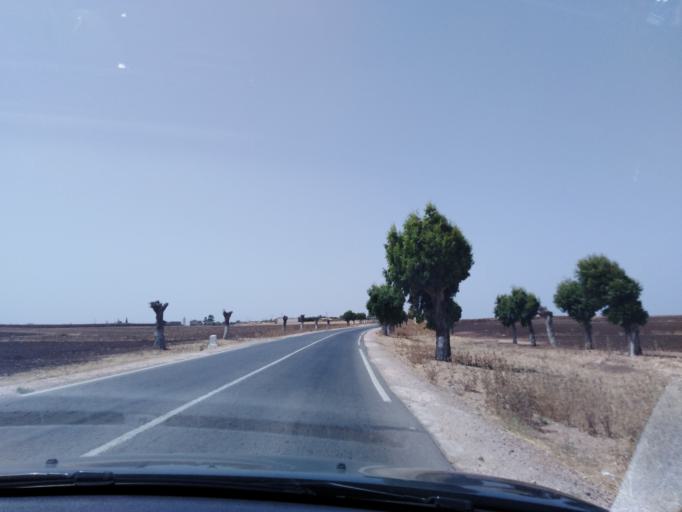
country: MA
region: Doukkala-Abda
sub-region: Safi
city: Youssoufia
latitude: 32.3791
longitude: -8.8269
